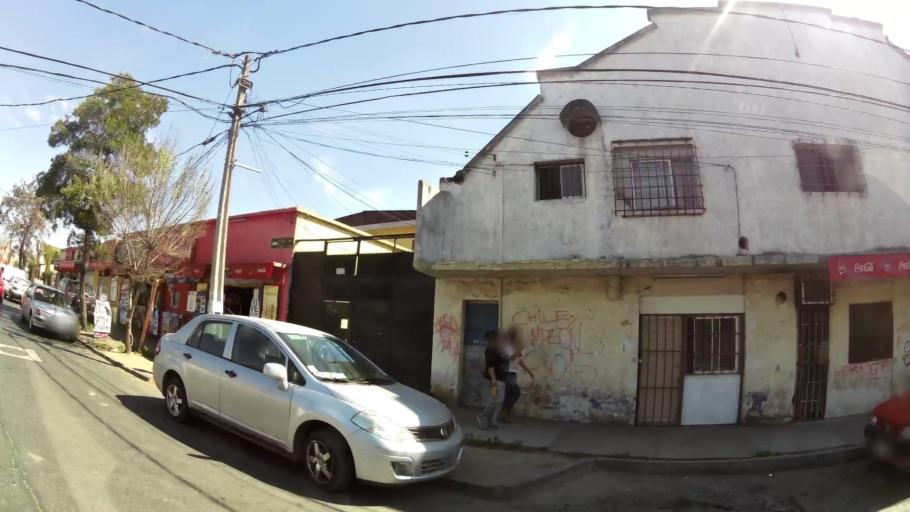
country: CL
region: Santiago Metropolitan
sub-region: Provincia de Santiago
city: Santiago
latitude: -33.5086
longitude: -70.6449
